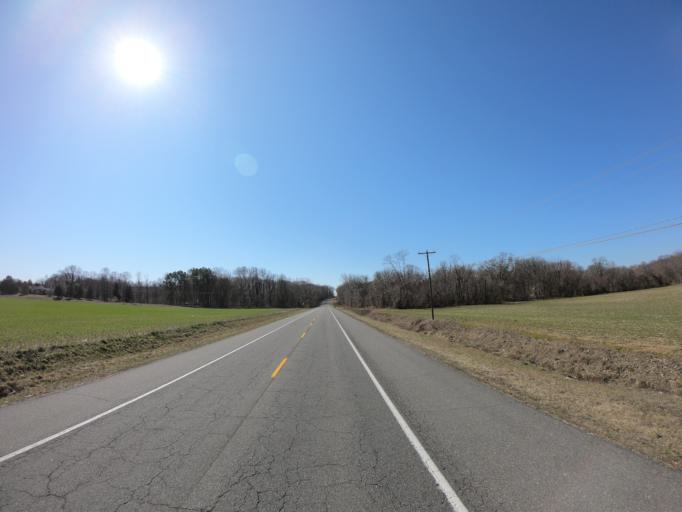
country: US
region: Delaware
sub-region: New Castle County
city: Townsend
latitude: 39.3507
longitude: -75.8393
